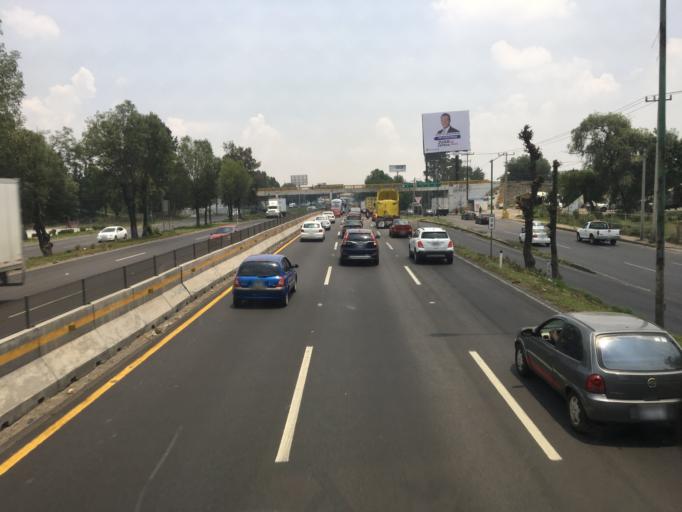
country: MX
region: Mexico
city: Cuautitlan
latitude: 19.6785
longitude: -99.2013
